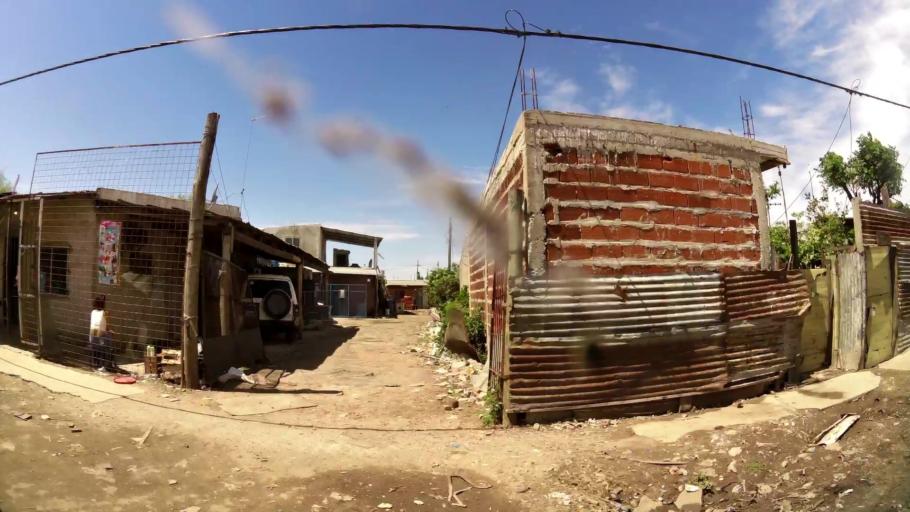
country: AR
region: Buenos Aires
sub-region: Partido de Quilmes
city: Quilmes
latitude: -34.7428
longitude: -58.3073
